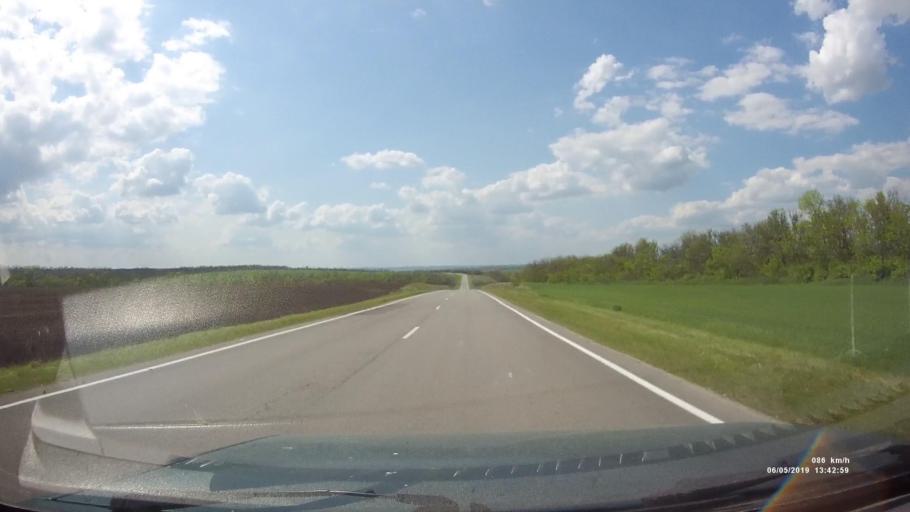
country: RU
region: Rostov
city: Semikarakorsk
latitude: 47.6598
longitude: 40.6472
